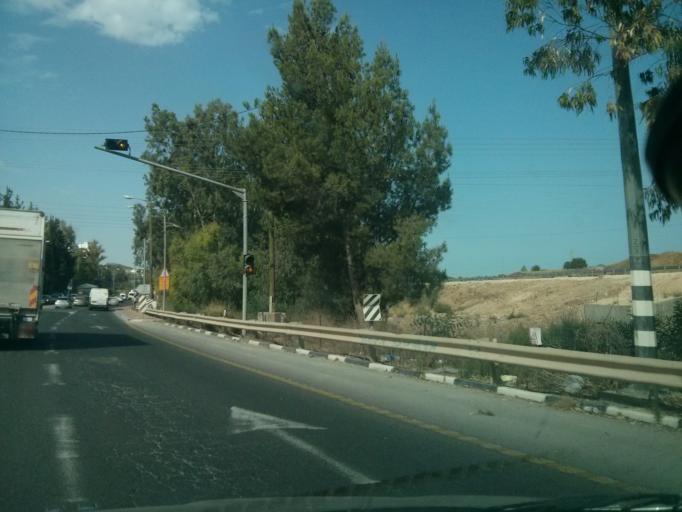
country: IL
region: Jerusalem
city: Bet Shemesh
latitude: 31.7634
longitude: 34.9953
